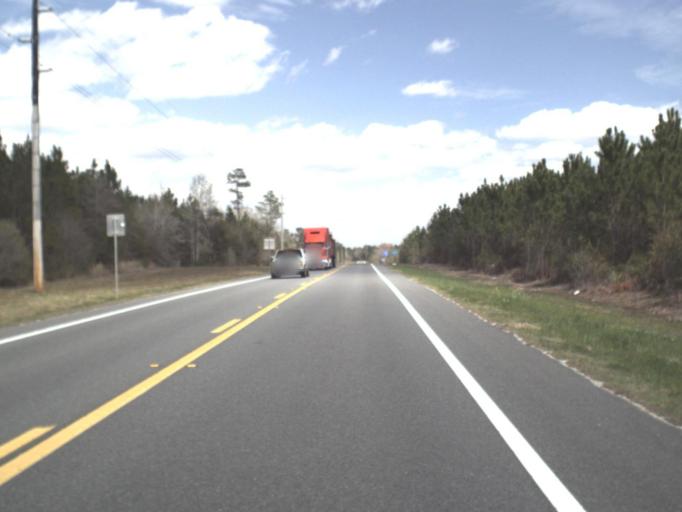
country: US
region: Florida
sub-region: Gadsden County
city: Quincy
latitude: 30.3919
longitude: -84.6817
